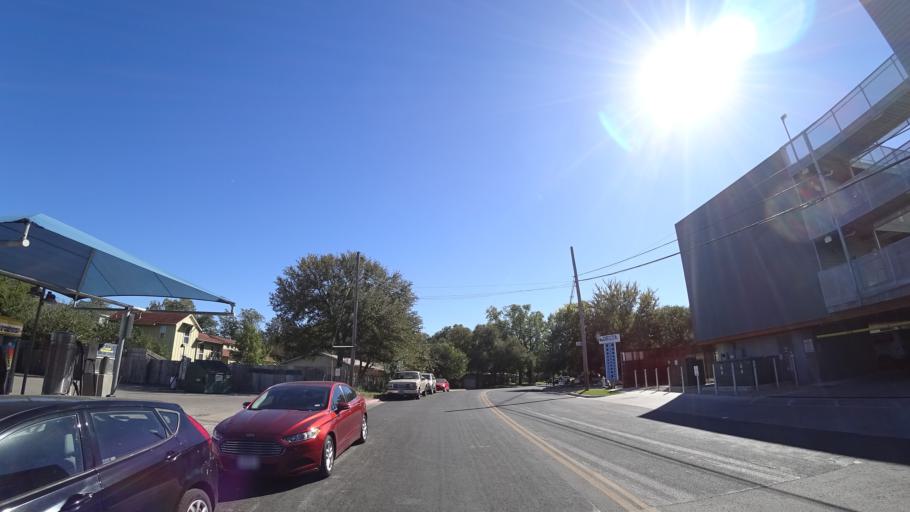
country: US
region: Texas
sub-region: Travis County
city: Rollingwood
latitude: 30.2470
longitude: -97.7751
